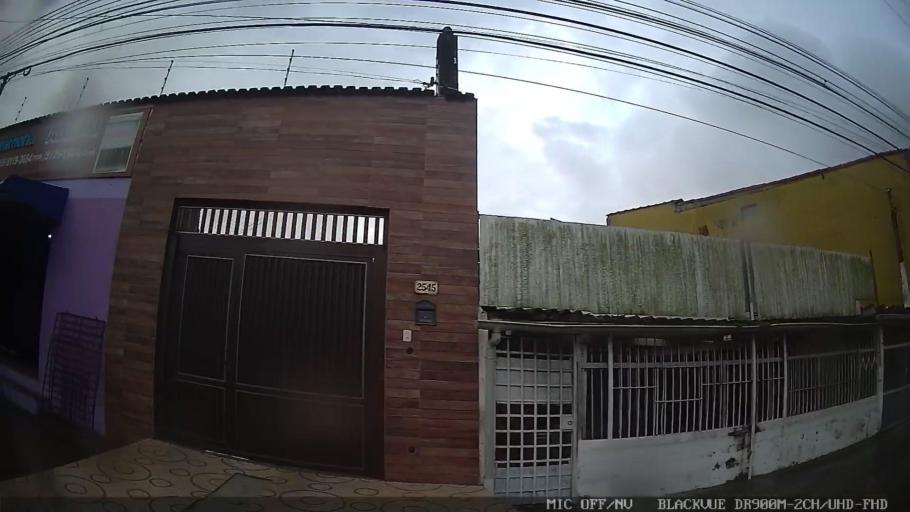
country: BR
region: Sao Paulo
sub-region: Itanhaem
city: Itanhaem
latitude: -24.1712
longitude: -46.7732
